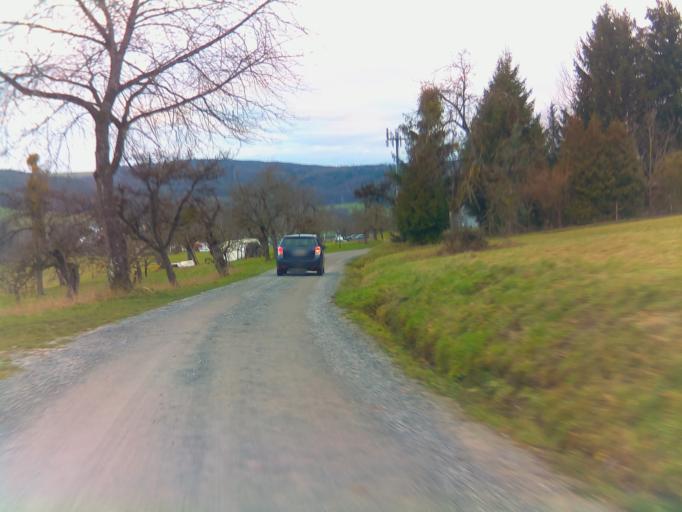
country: DE
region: Bavaria
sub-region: Regierungsbezirk Unterfranken
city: Hausen
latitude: 49.8784
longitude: 9.2045
